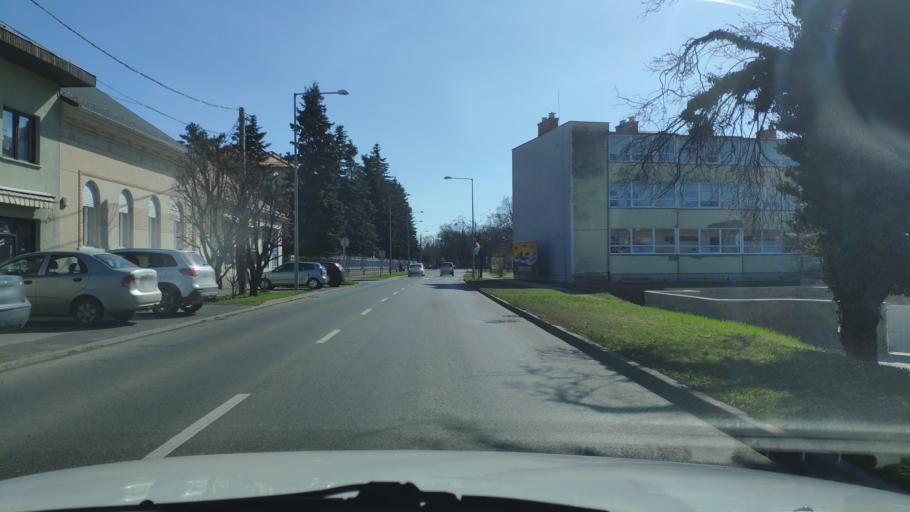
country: HU
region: Zala
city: Nagykanizsa
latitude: 46.4534
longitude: 16.9977
